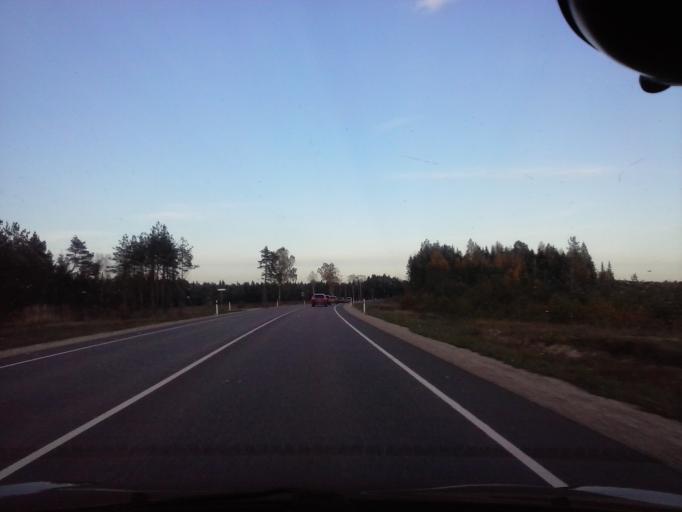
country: EE
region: Harju
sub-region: Nissi vald
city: Turba
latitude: 58.9779
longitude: 23.9573
